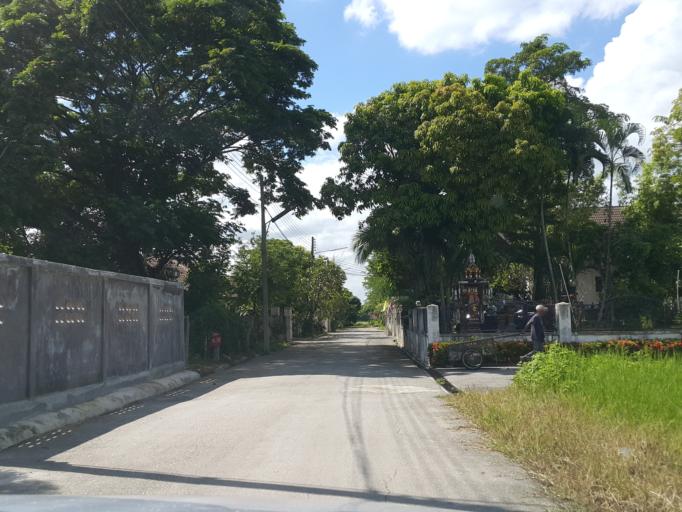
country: TH
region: Chiang Mai
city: San Kamphaeng
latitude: 18.7525
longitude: 99.1227
